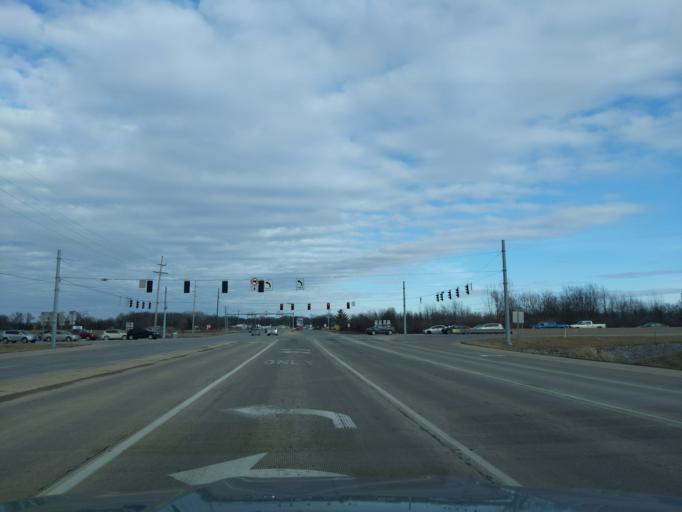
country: US
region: Indiana
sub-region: Tippecanoe County
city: Shadeland
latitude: 40.3867
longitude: -86.9196
